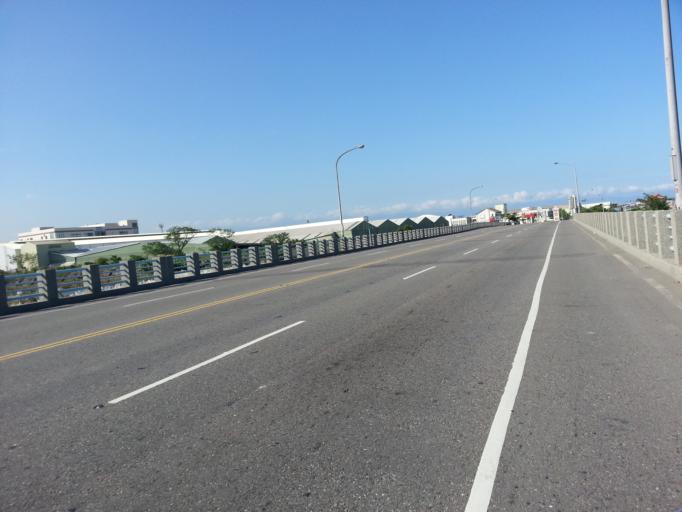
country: TW
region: Taiwan
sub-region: Yilan
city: Yilan
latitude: 24.6311
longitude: 121.8319
